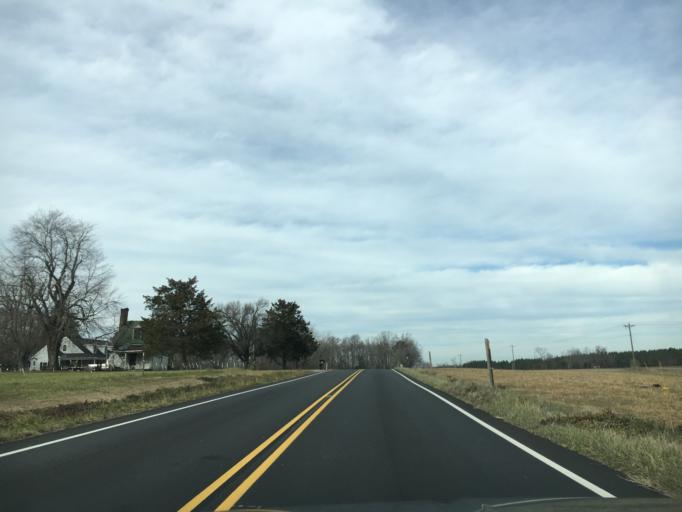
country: US
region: Virginia
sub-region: Goochland County
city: Goochland
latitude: 37.8126
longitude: -77.8696
